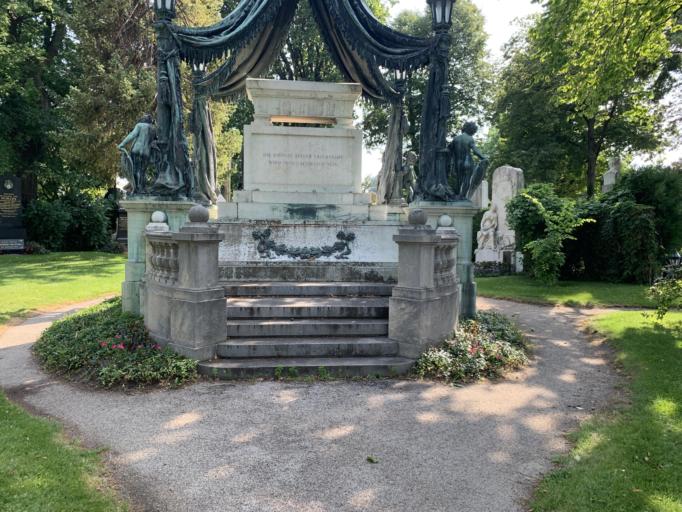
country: AT
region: Lower Austria
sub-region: Politischer Bezirk Wien-Umgebung
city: Schwechat
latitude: 48.1524
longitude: 16.4394
